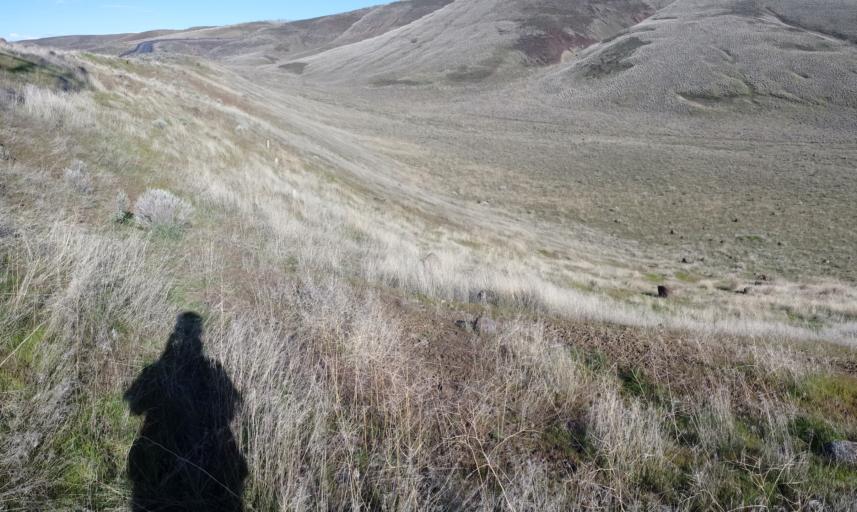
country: US
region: Washington
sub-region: Grant County
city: Quincy
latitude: 47.2386
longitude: -119.9883
